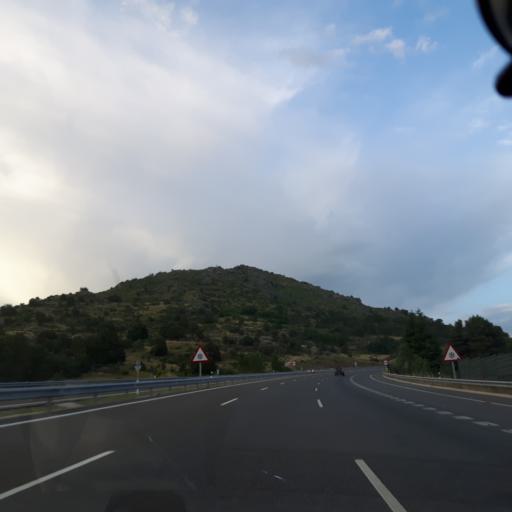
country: ES
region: Castille and Leon
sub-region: Provincia de Salamanca
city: Fresnedoso
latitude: 40.4326
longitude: -5.6950
